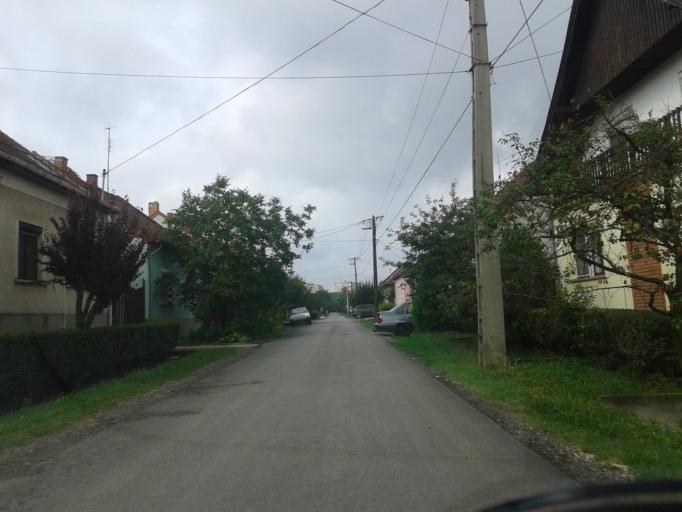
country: HU
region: Csongrad
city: Szeged
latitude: 46.2653
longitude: 20.1812
